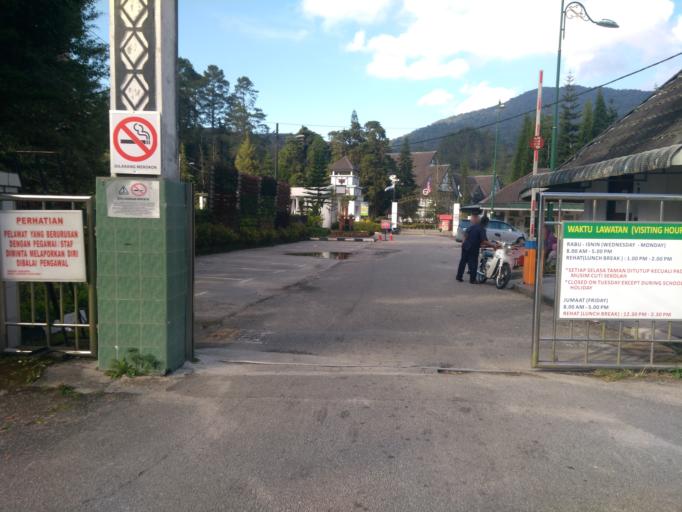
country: MY
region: Pahang
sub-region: Cameron Highlands
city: Tanah Rata
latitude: 4.4677
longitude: 101.3844
